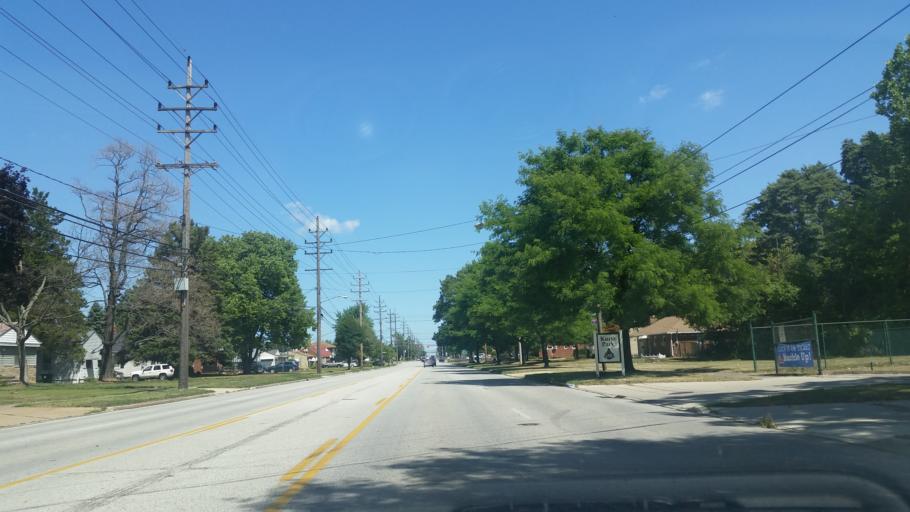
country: US
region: Ohio
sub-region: Cuyahoga County
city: Brook Park
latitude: 41.3921
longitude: -81.7844
